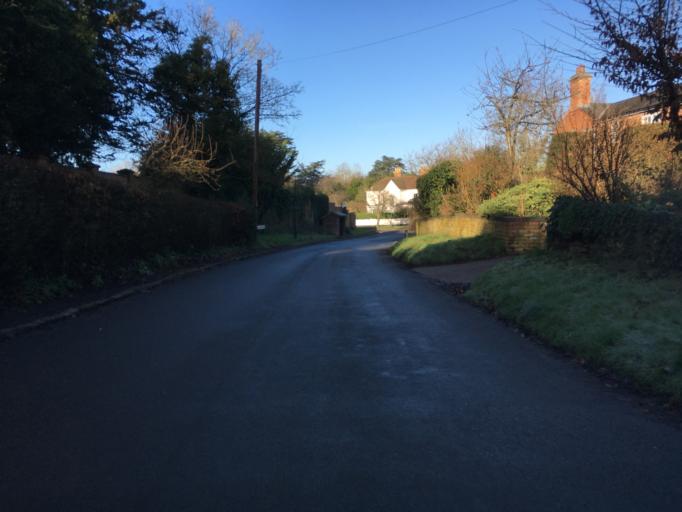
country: GB
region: England
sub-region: Warwickshire
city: Stratford-upon-Avon
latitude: 52.2057
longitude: -1.6575
